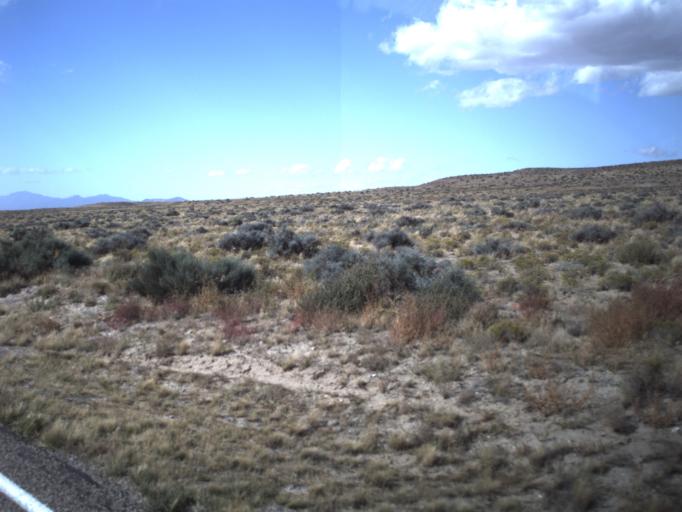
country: US
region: Utah
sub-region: Beaver County
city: Milford
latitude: 38.7591
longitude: -112.9429
